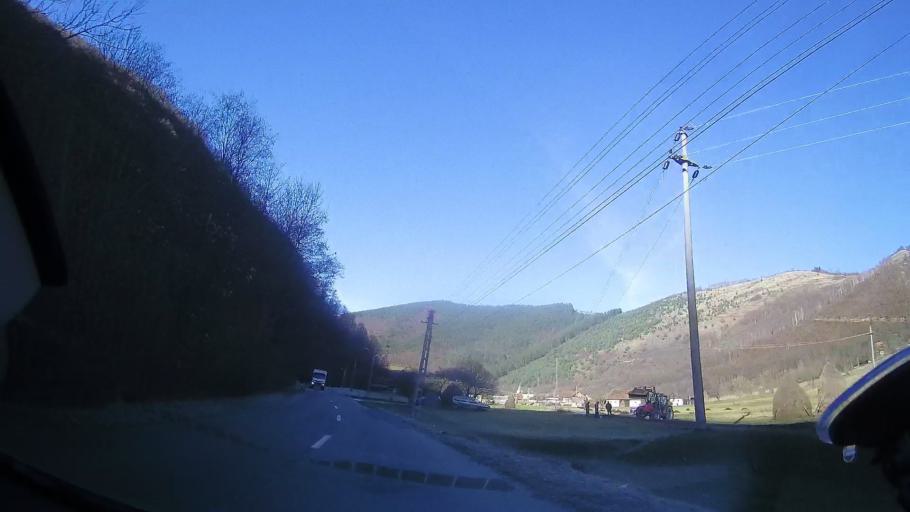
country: RO
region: Bihor
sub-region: Comuna Bulz
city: Bulz
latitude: 46.9089
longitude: 22.6790
